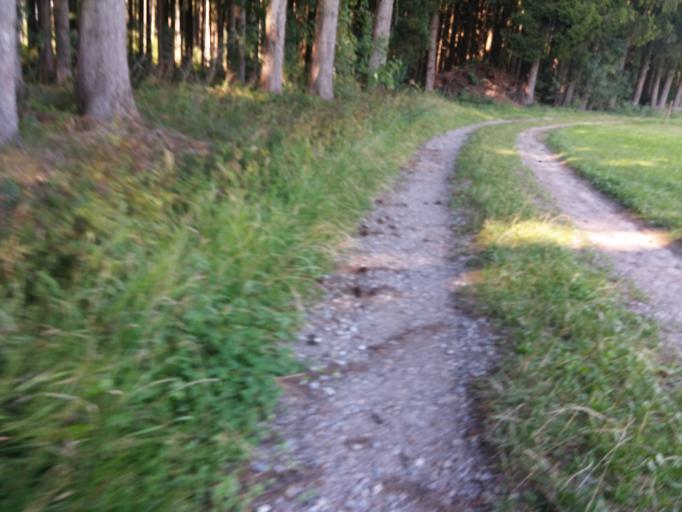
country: DE
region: Baden-Wuerttemberg
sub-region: Tuebingen Region
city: Leutkirch im Allgau
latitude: 47.7788
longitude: 10.0718
